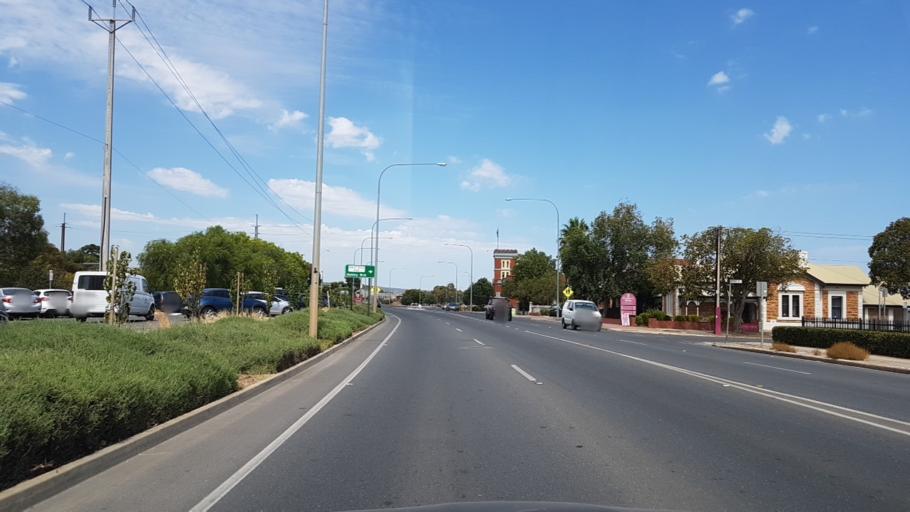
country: AU
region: South Australia
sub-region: City of West Torrens
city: Thebarton
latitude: -34.9215
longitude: 138.5792
